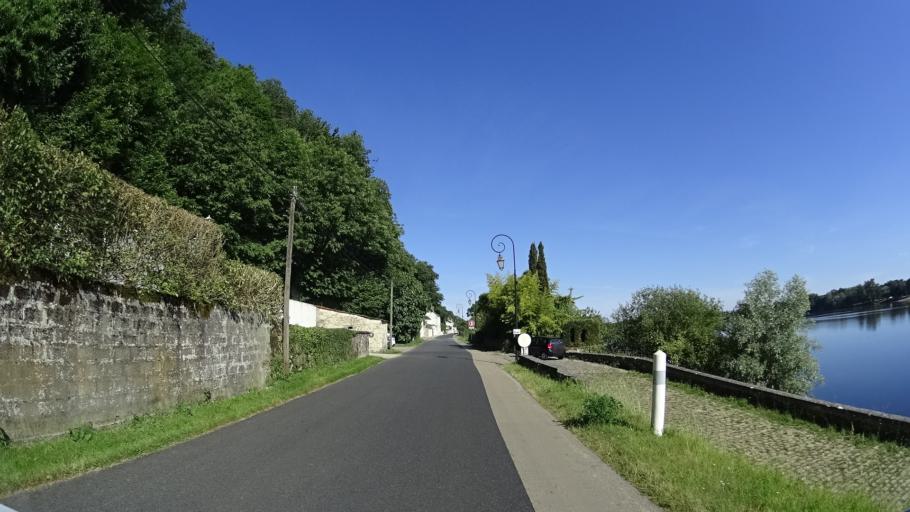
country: FR
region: Pays de la Loire
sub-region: Departement de Maine-et-Loire
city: Saint-Martin-de-la-Place
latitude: 47.3049
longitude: -0.1474
